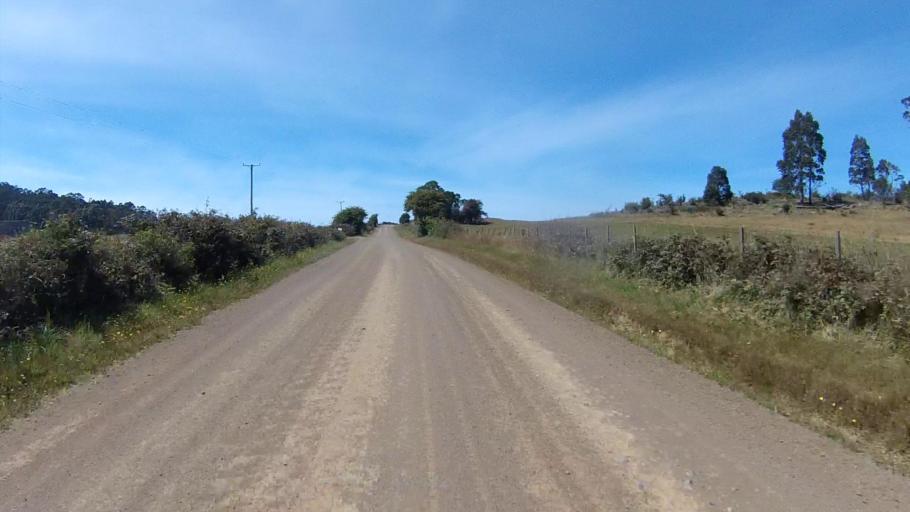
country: AU
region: Tasmania
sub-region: Sorell
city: Sorell
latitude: -42.7067
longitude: 147.7457
